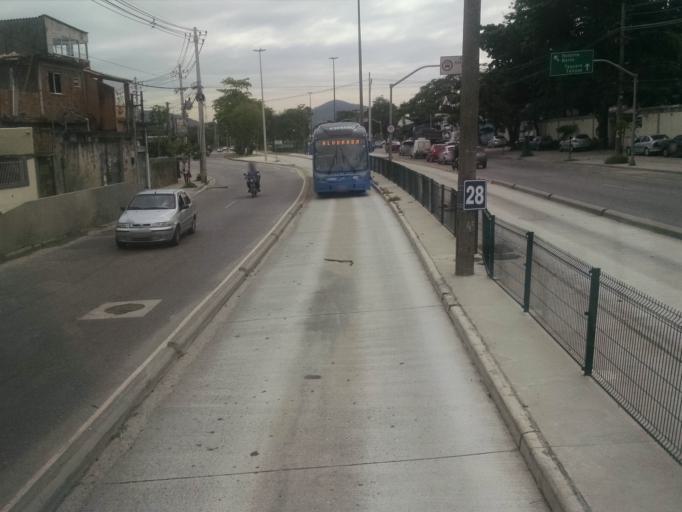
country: BR
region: Rio de Janeiro
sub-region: Sao Joao De Meriti
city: Sao Joao de Meriti
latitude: -22.9464
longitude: -43.3719
